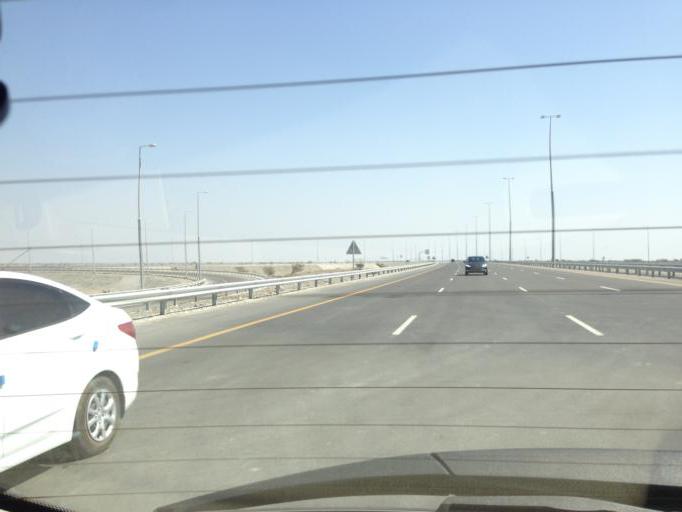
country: OM
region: Al Batinah
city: Bayt al `Awabi
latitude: 23.5275
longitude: 57.6638
